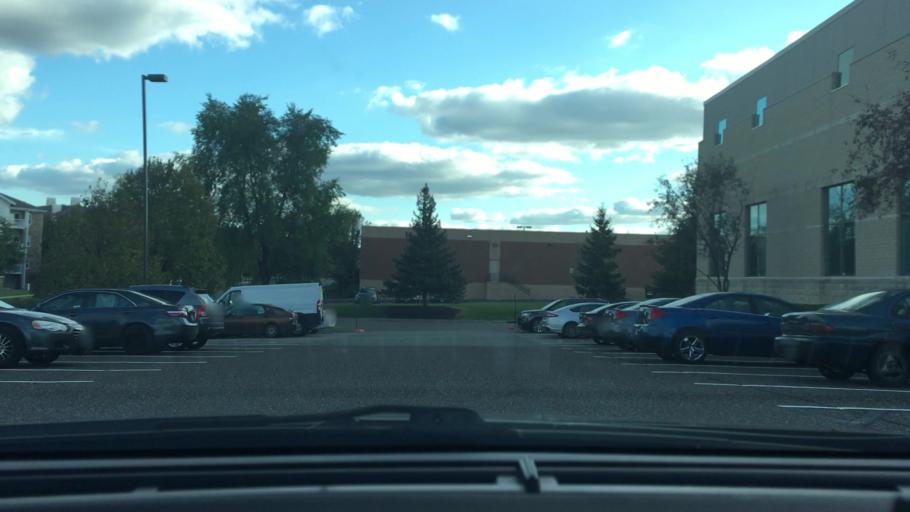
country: US
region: Minnesota
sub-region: Hennepin County
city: Maple Grove
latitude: 45.0671
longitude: -93.4400
